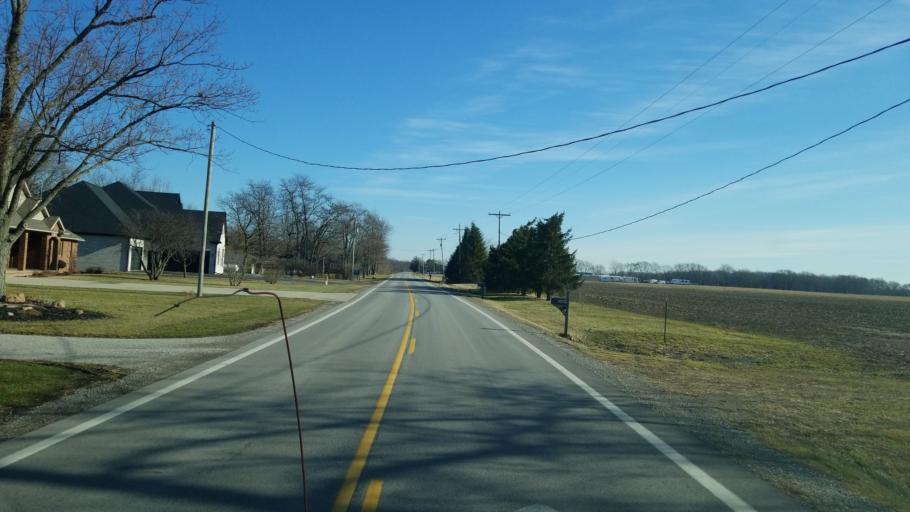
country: US
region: Ohio
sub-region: Henry County
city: Liberty Center
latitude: 41.4153
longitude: -83.9124
